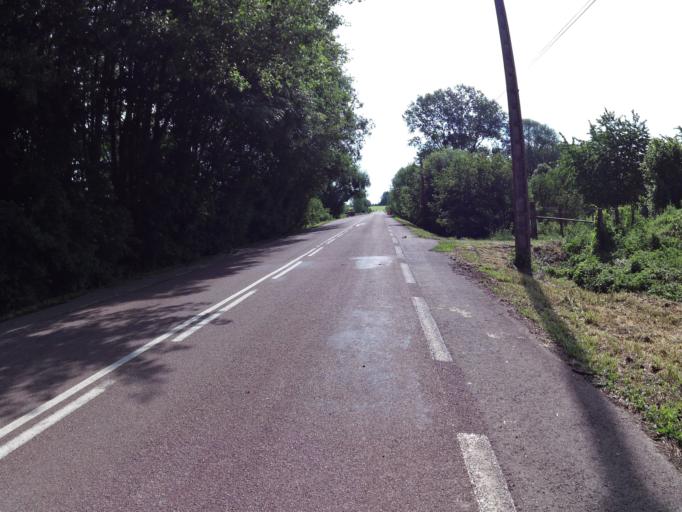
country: FR
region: Champagne-Ardenne
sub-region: Departement de l'Aube
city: Verrieres
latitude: 48.2676
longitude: 4.1745
